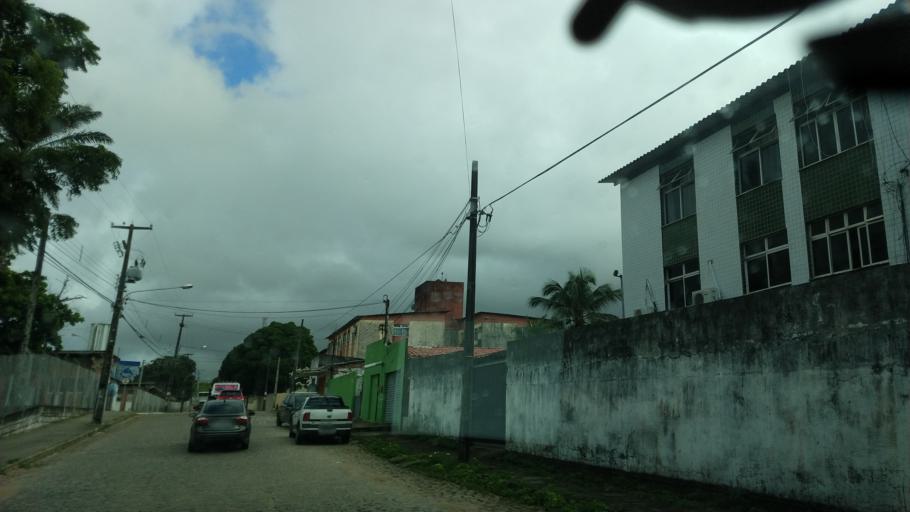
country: BR
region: Rio Grande do Norte
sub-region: Natal
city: Natal
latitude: -5.8599
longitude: -35.2110
